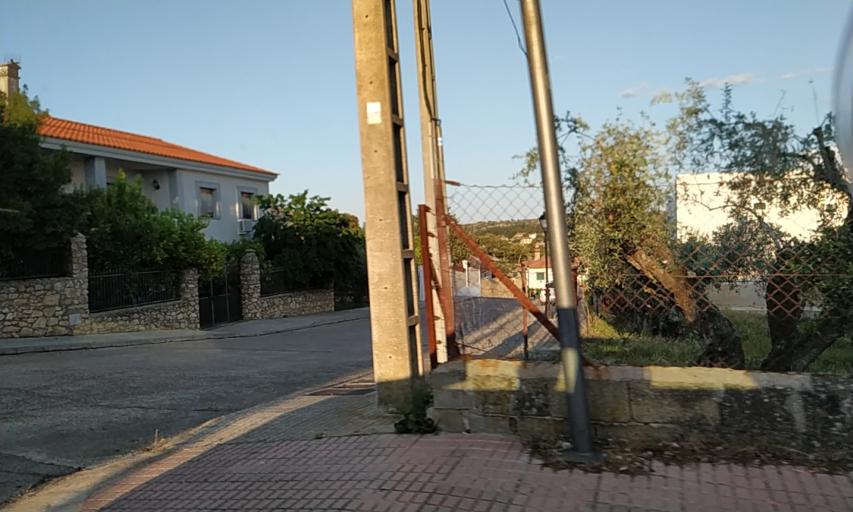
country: ES
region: Extremadura
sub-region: Provincia de Caceres
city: Valencia de Alcantara
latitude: 39.4050
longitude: -7.2494
